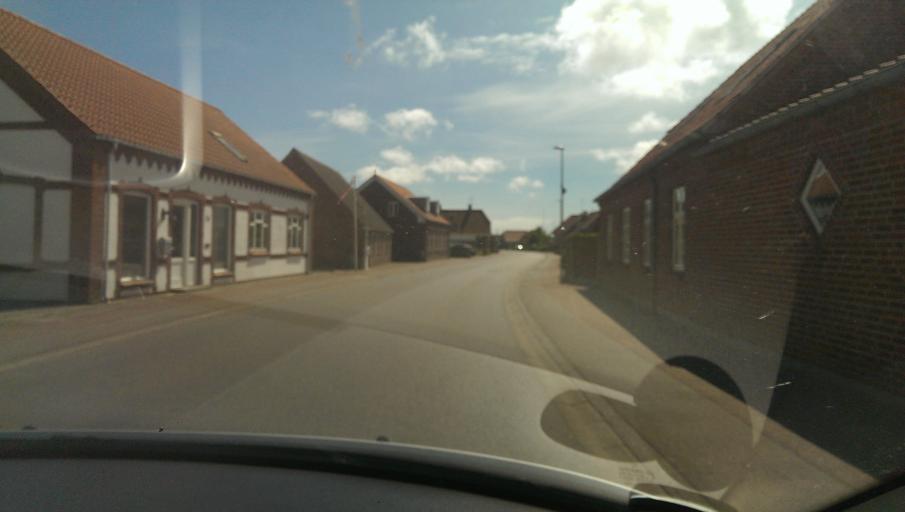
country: DK
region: Central Jutland
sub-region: Ringkobing-Skjern Kommune
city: Ringkobing
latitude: 56.1253
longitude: 8.1777
